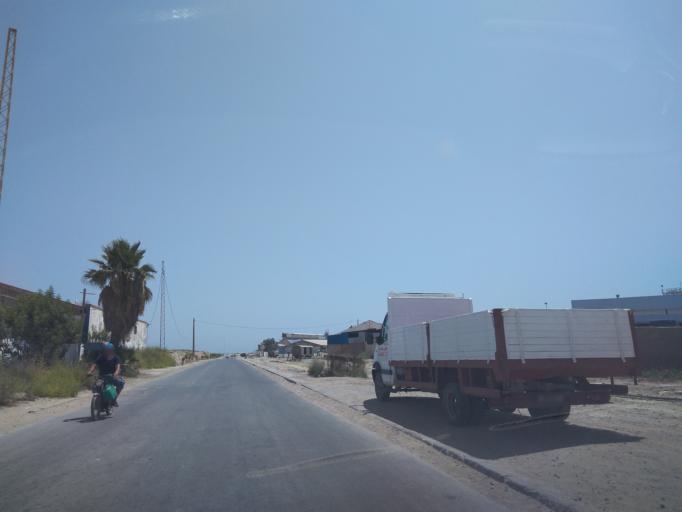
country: TN
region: Safaqis
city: Sfax
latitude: 34.7326
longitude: 10.7710
